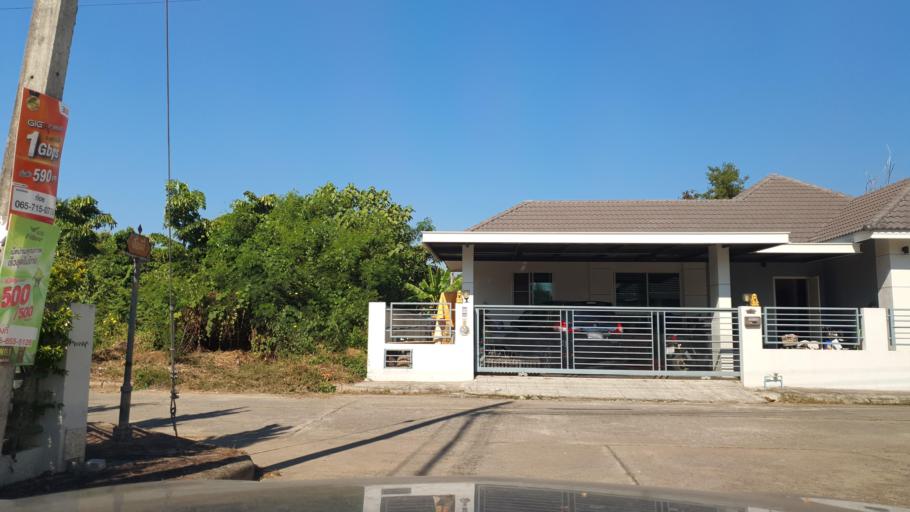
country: TH
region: Chiang Mai
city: Hang Dong
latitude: 18.6959
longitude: 98.9354
